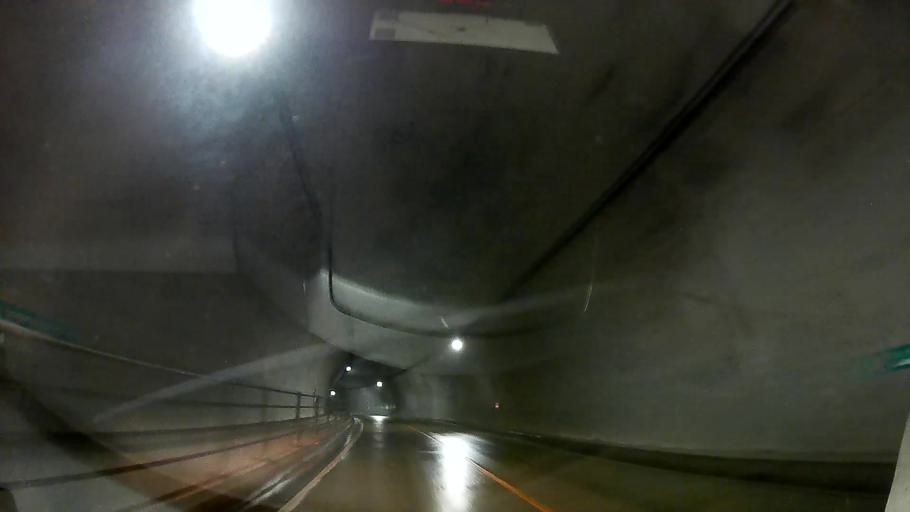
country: JP
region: Oita
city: Tsukawaki
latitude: 33.1828
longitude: 131.0322
